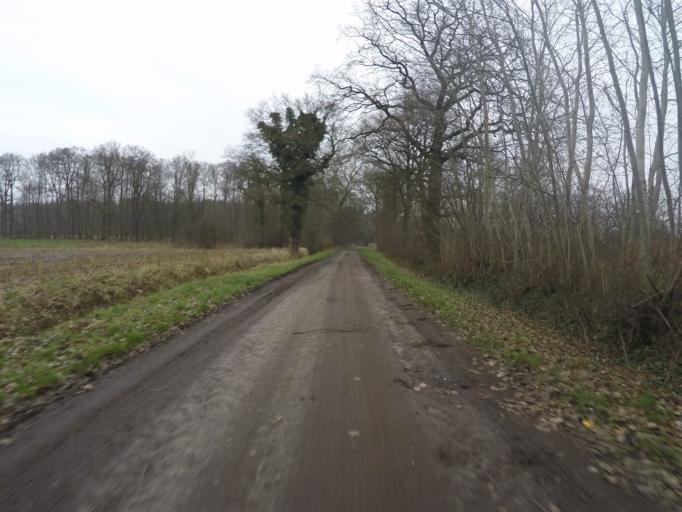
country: DE
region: Schleswig-Holstein
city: Borstel-Hohenraden
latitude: 53.7061
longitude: 9.8467
